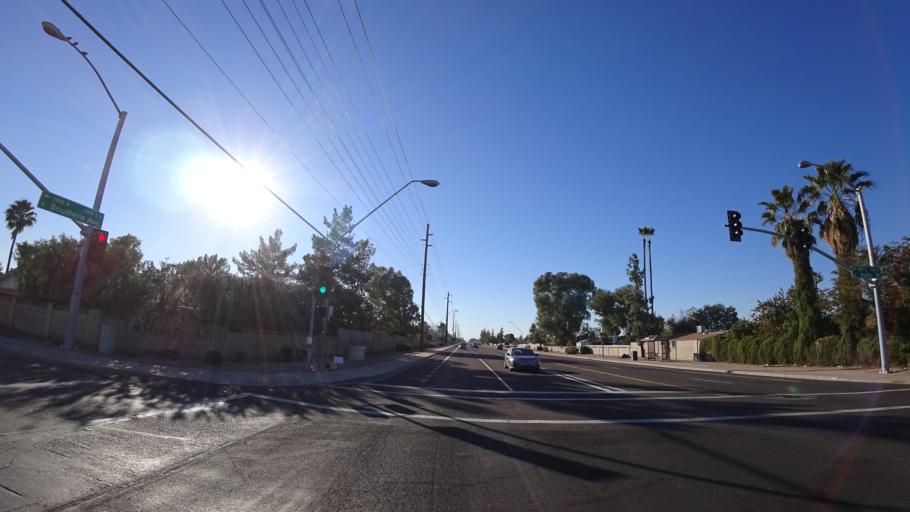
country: US
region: Arizona
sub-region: Maricopa County
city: Mesa
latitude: 33.3934
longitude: -111.7970
